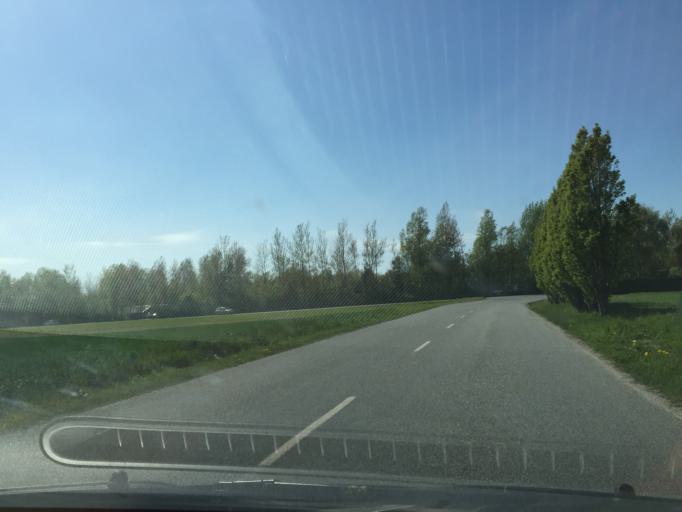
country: DK
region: Zealand
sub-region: Lolland Kommune
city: Rodbyhavn
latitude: 54.6717
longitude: 11.3417
